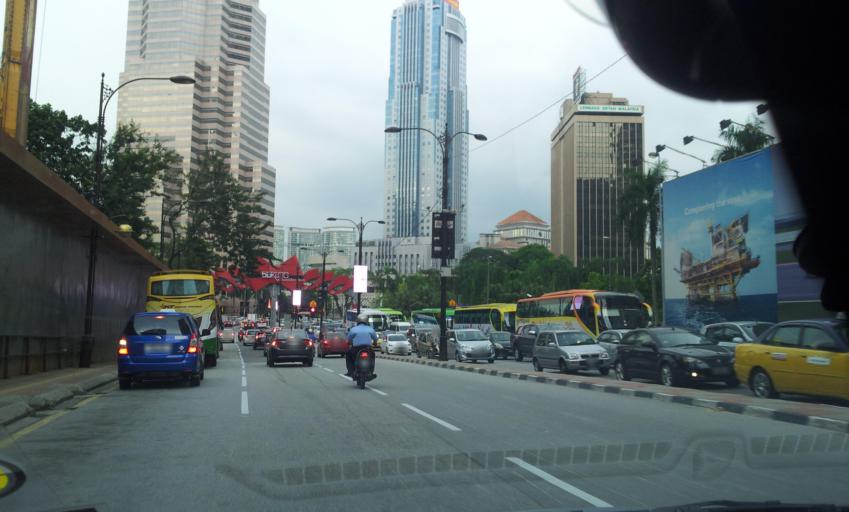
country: MY
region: Kuala Lumpur
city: Kuala Lumpur
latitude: 3.1572
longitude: 101.7107
